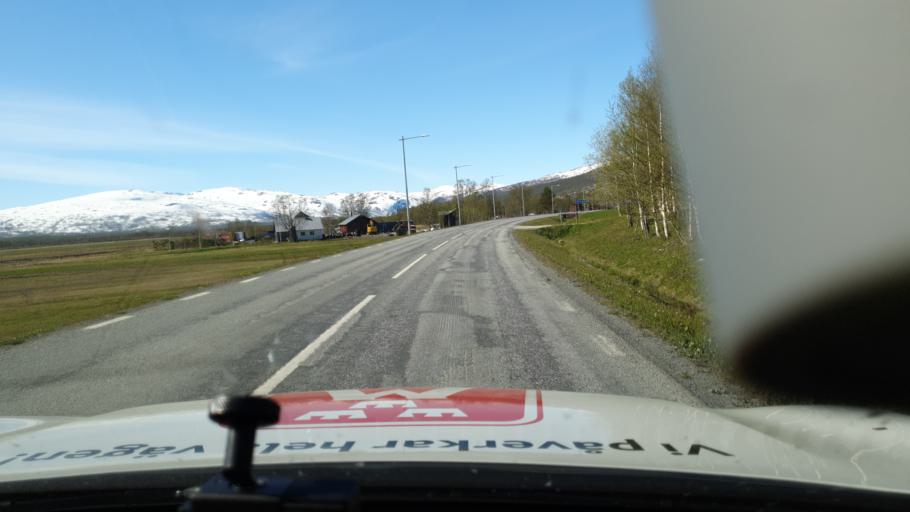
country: NO
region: Nordland
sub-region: Rana
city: Mo i Rana
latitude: 65.8062
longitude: 15.0895
